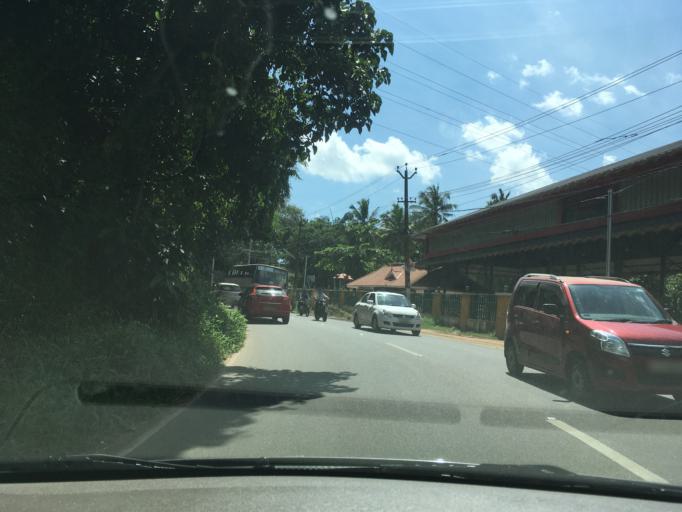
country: IN
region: Kerala
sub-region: Thiruvananthapuram
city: Nedumangad
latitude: 8.6035
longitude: 76.9969
